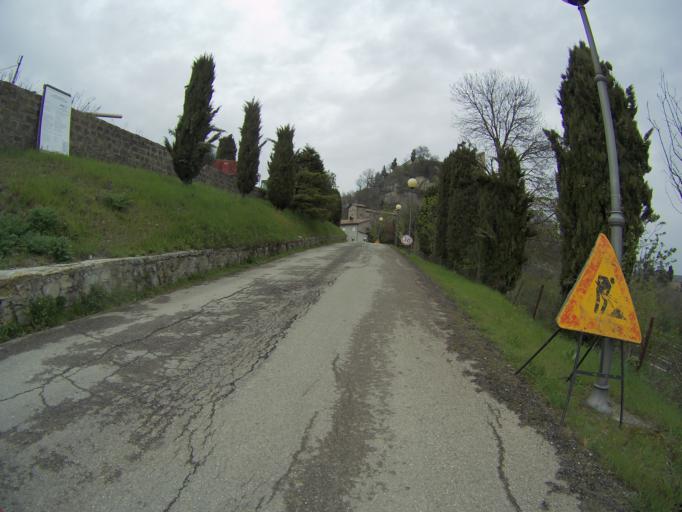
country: IT
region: Emilia-Romagna
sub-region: Provincia di Reggio Emilia
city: Ciano d'Enza
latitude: 44.5742
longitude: 10.4554
